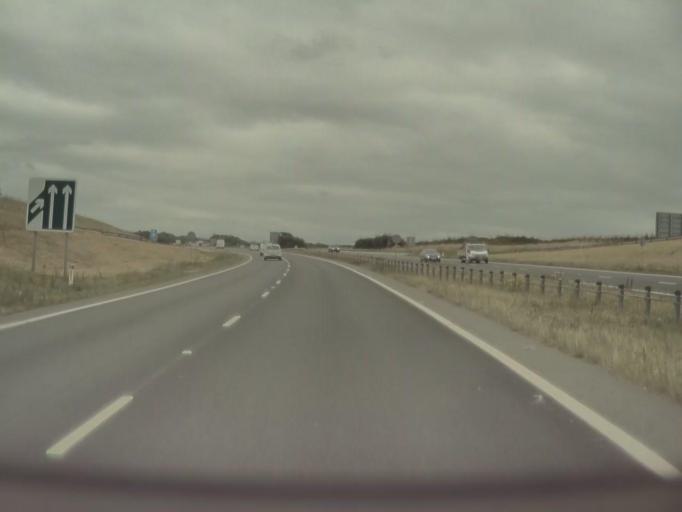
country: GB
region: Wales
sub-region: Anglesey
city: Llanfachraeth
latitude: 53.2755
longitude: -4.5138
